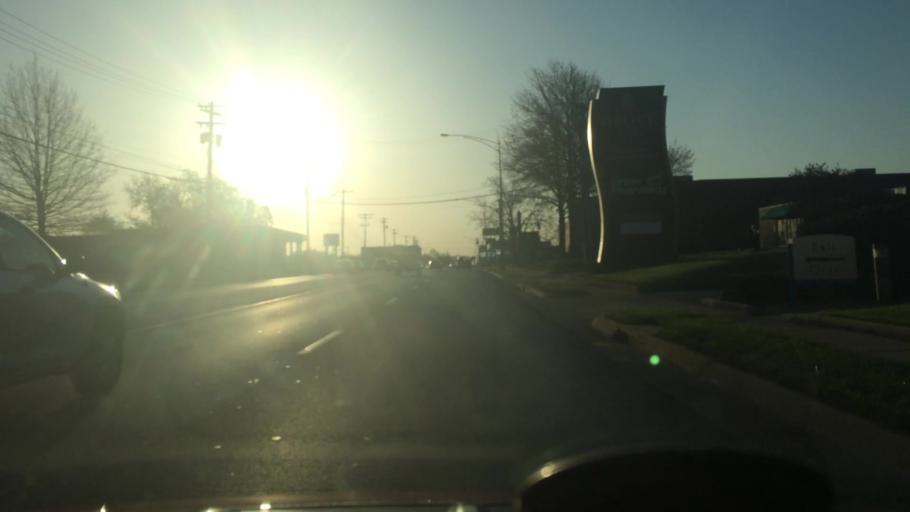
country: US
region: Missouri
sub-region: Greene County
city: Springfield
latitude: 37.1816
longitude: -93.2683
